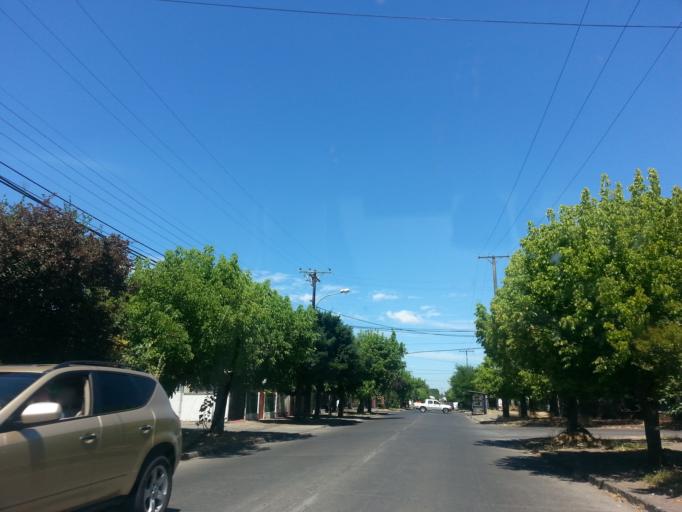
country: CL
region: Biobio
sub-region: Provincia de Nuble
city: Chillan
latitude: -36.6052
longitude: -72.0831
